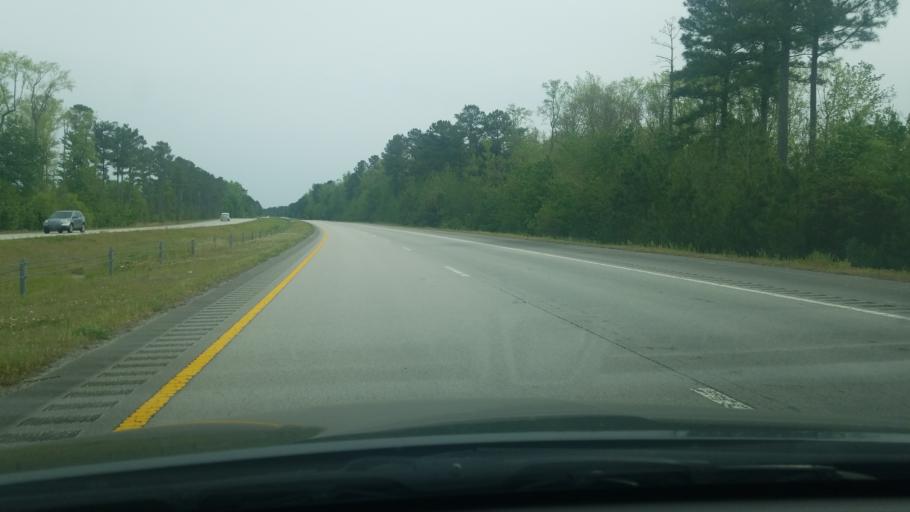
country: US
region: North Carolina
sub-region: Craven County
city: River Bend
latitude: 35.1090
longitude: -77.1625
